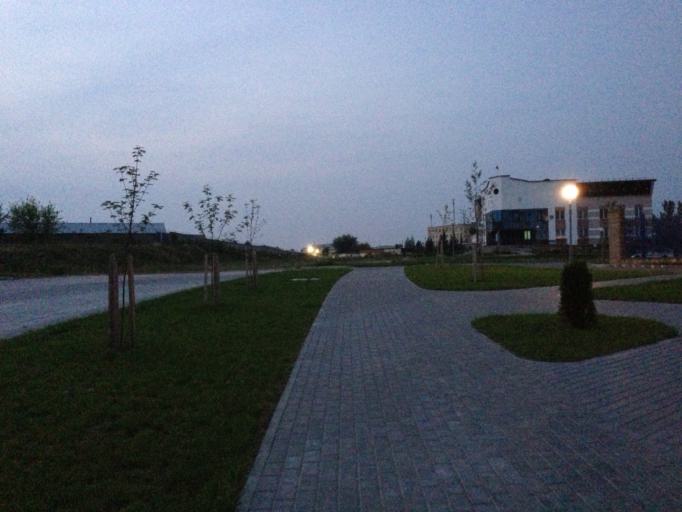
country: BY
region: Grodnenskaya
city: Hrodna
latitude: 53.7010
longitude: 23.8252
